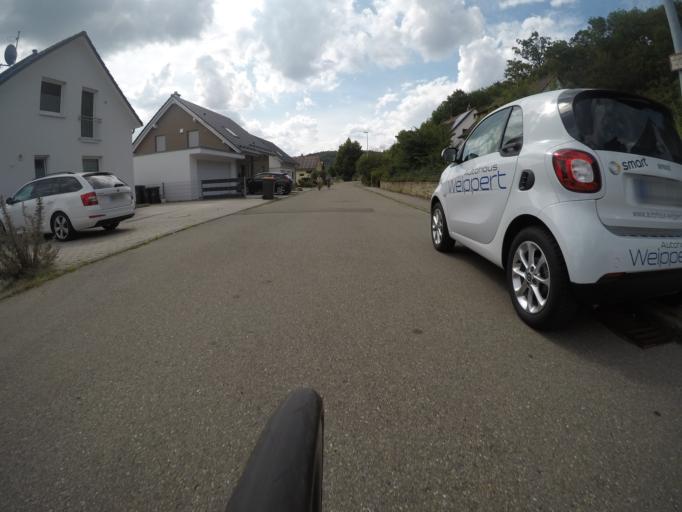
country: DE
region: Baden-Wuerttemberg
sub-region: Regierungsbezirk Stuttgart
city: Weil der Stadt
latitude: 48.7283
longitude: 8.8884
